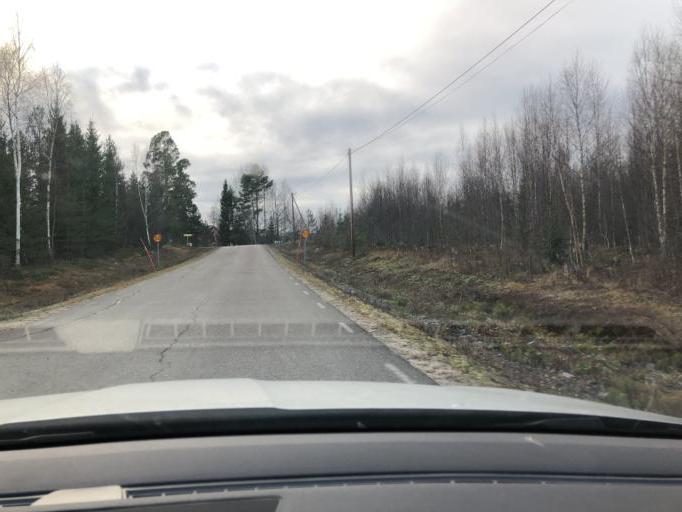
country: SE
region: Gaevleborg
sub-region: Hudiksvalls Kommun
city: Sorforsa
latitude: 61.7029
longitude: 16.9394
